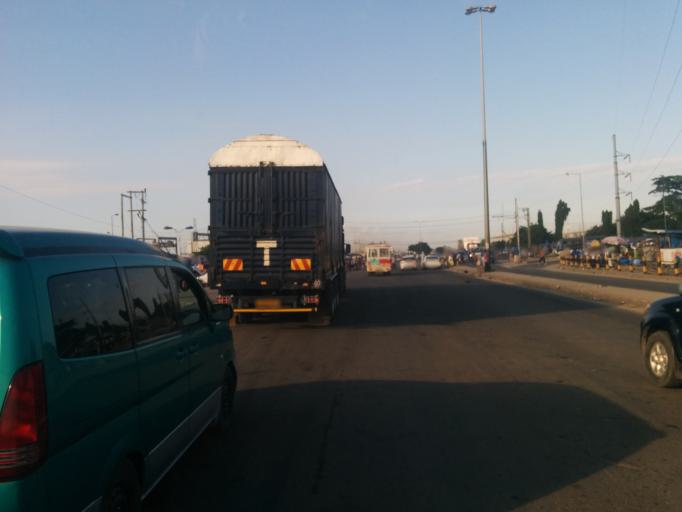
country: TZ
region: Dar es Salaam
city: Magomeni
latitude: -6.7917
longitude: 39.2085
